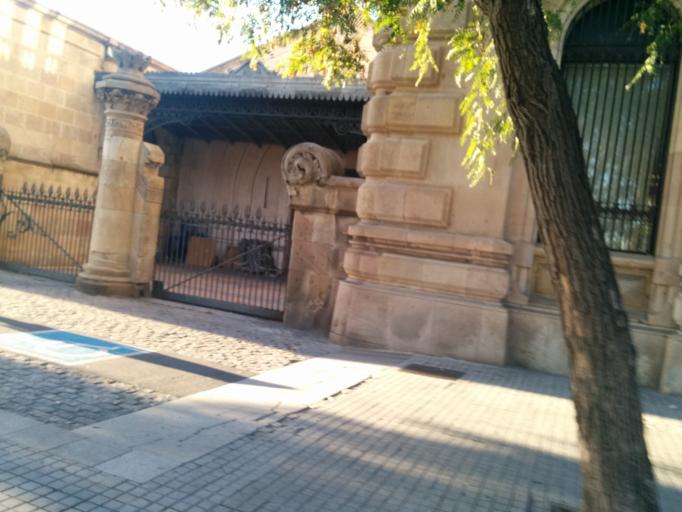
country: ES
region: Catalonia
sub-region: Provincia de Barcelona
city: Ciutat Vella
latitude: 41.3753
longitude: 2.1777
